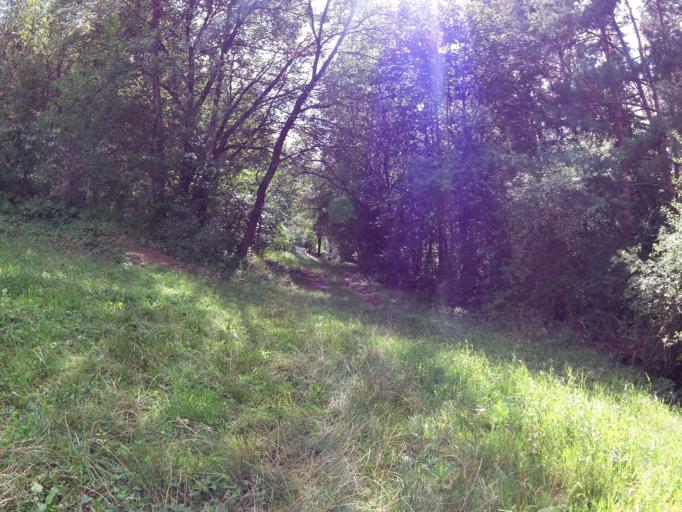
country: DE
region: Bavaria
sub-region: Regierungsbezirk Unterfranken
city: Erlabrunn
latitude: 49.8394
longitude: 9.8418
